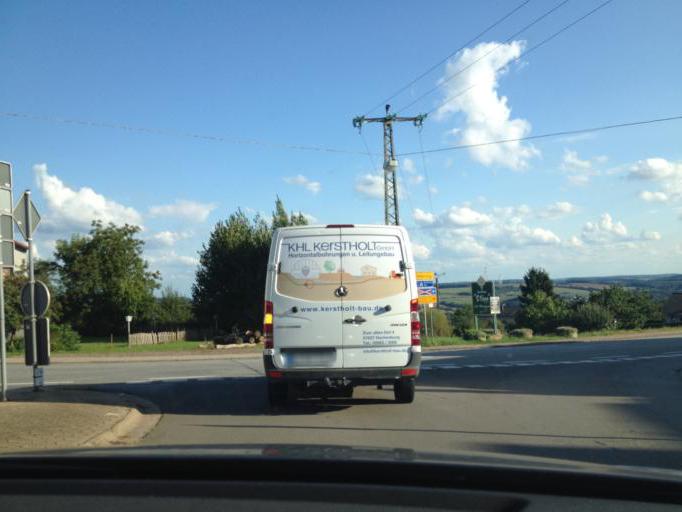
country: DE
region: Saarland
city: Eppelborn
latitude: 49.4724
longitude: 6.9626
